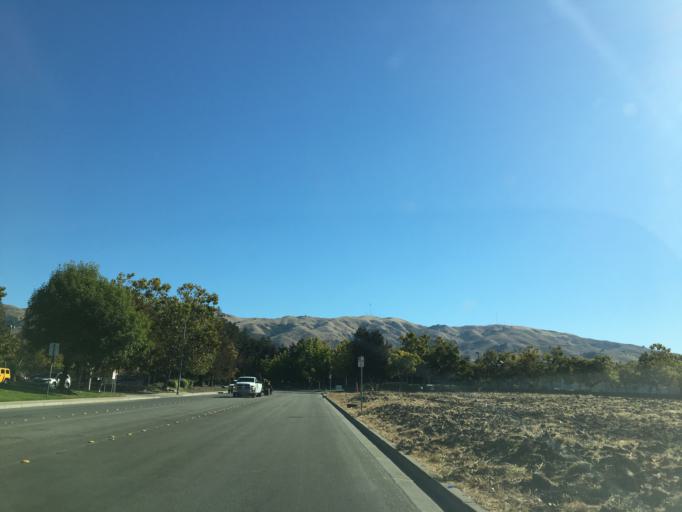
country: US
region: California
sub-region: Alameda County
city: Fremont
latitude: 37.5002
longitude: -121.9329
